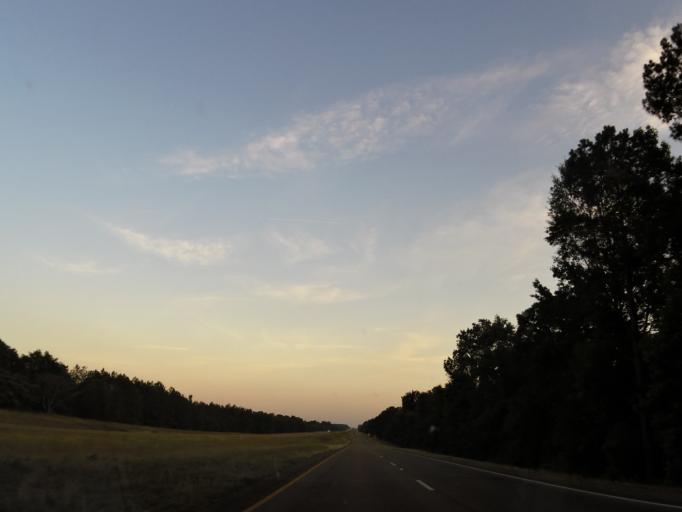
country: US
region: Mississippi
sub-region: Kemper County
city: De Kalb
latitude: 32.9012
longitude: -88.5097
